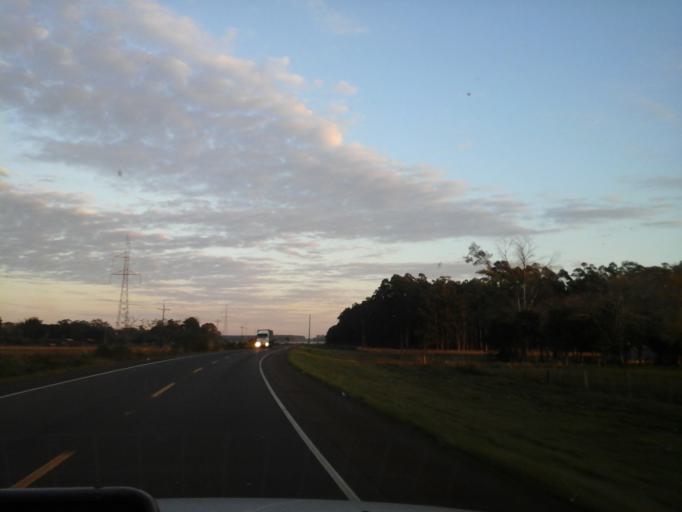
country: PY
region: Itapua
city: General Delgado
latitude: -27.0725
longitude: -56.6039
